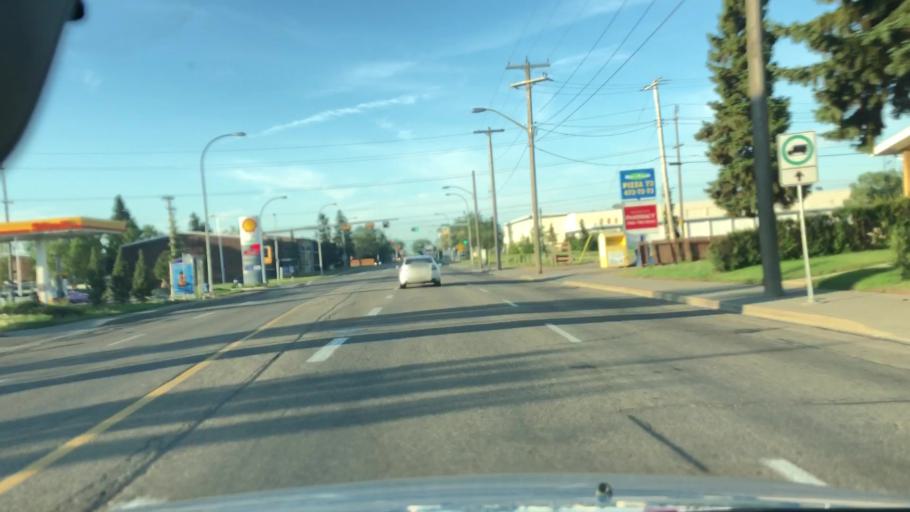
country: CA
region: Alberta
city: Edmonton
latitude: 53.5932
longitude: -113.5412
